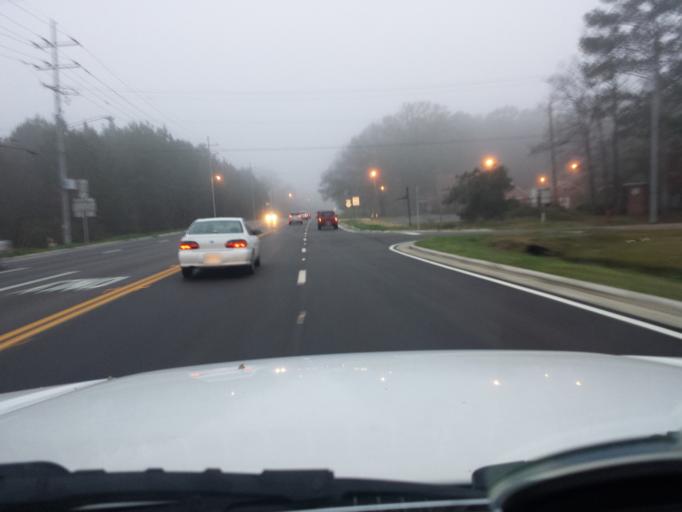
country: US
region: Mississippi
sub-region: Rankin County
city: Flowood
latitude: 32.3291
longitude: -90.0917
